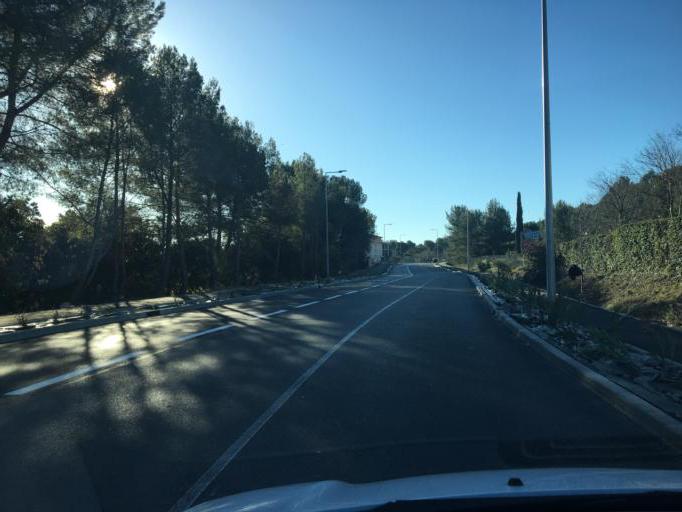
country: FR
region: Provence-Alpes-Cote d'Azur
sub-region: Departement des Bouches-du-Rhone
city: Cabries
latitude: 43.4838
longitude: 5.3639
